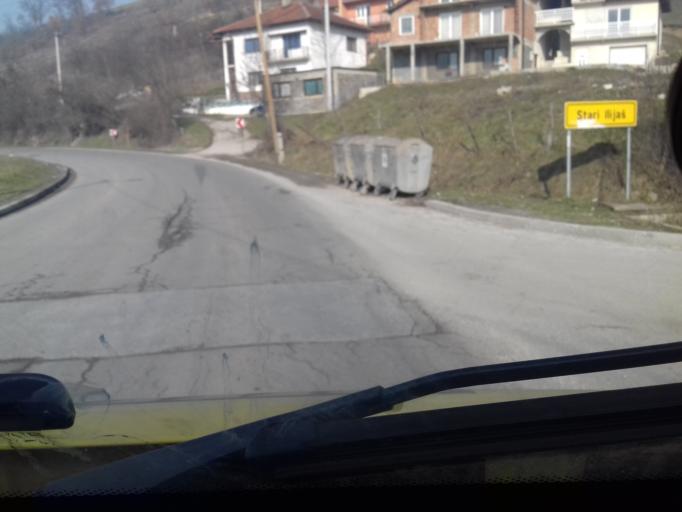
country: BA
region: Federation of Bosnia and Herzegovina
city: Ilijas
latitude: 43.9399
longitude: 18.2799
